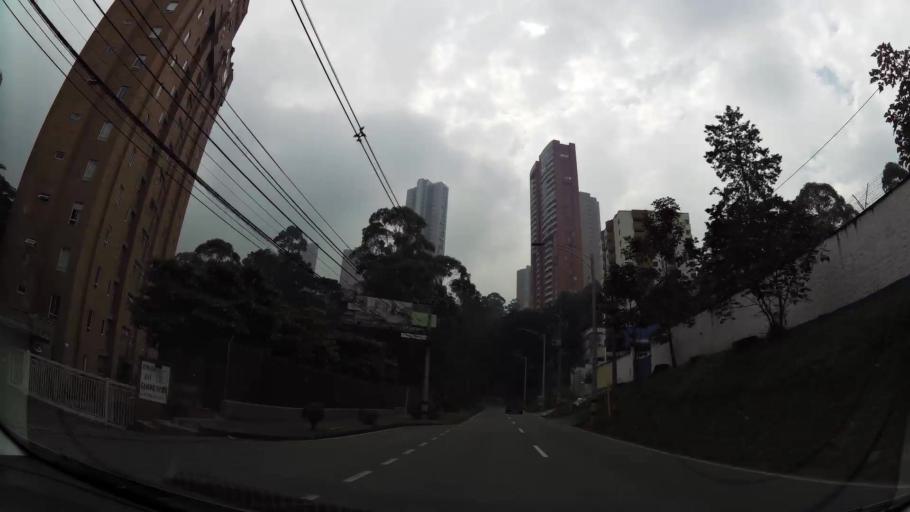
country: CO
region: Antioquia
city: Envigado
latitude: 6.1841
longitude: -75.5626
